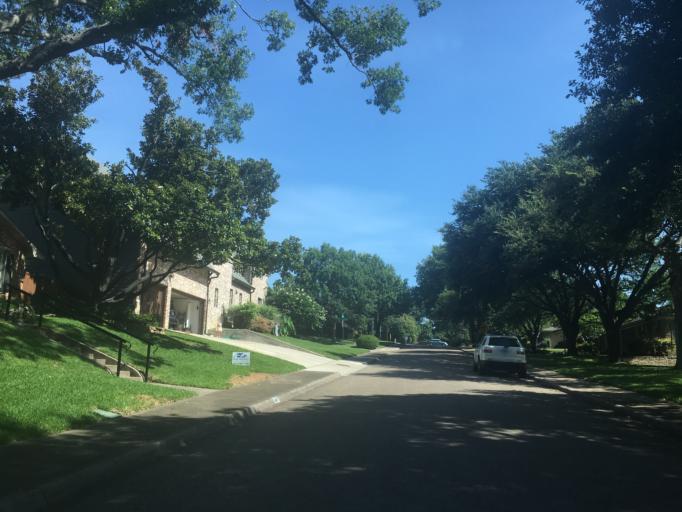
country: US
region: Texas
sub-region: Dallas County
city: Richardson
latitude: 32.8776
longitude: -96.7263
